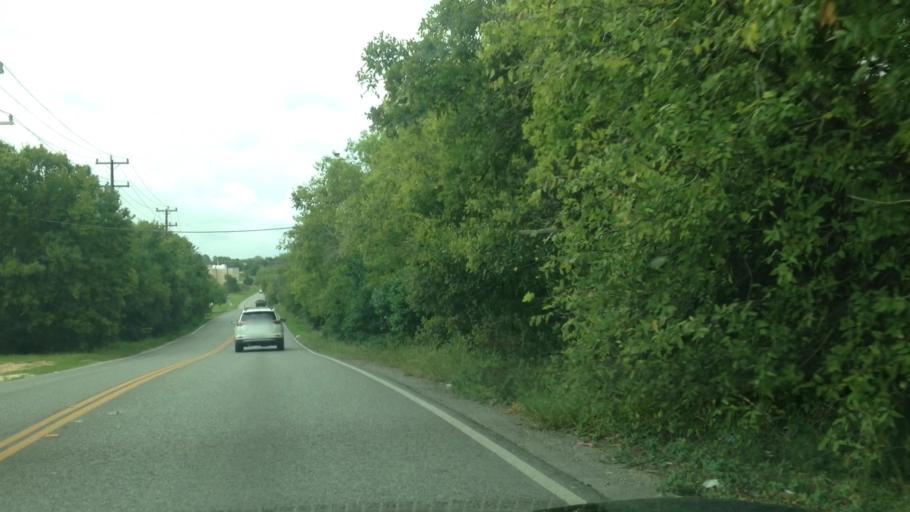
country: US
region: Texas
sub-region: Bexar County
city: Windcrest
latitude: 29.5775
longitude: -98.4010
